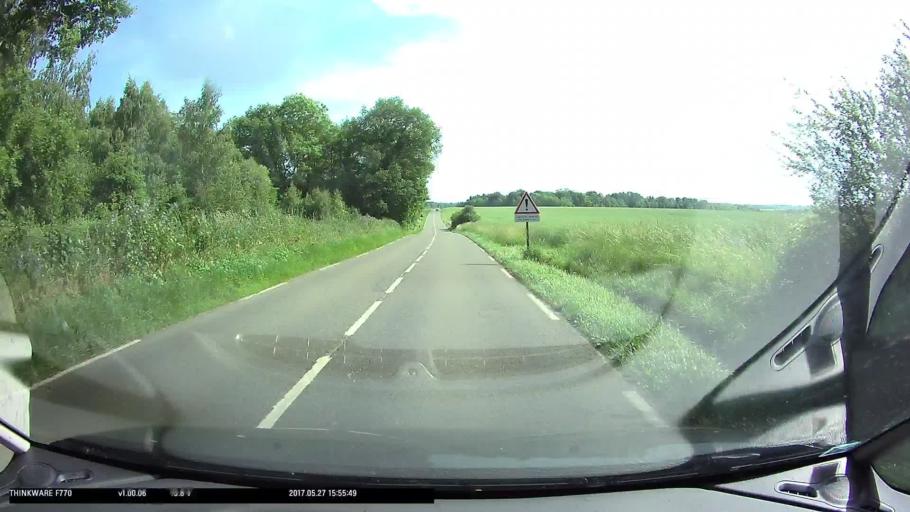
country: FR
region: Ile-de-France
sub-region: Departement du Val-d'Oise
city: Marines
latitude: 49.1218
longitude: 1.9817
